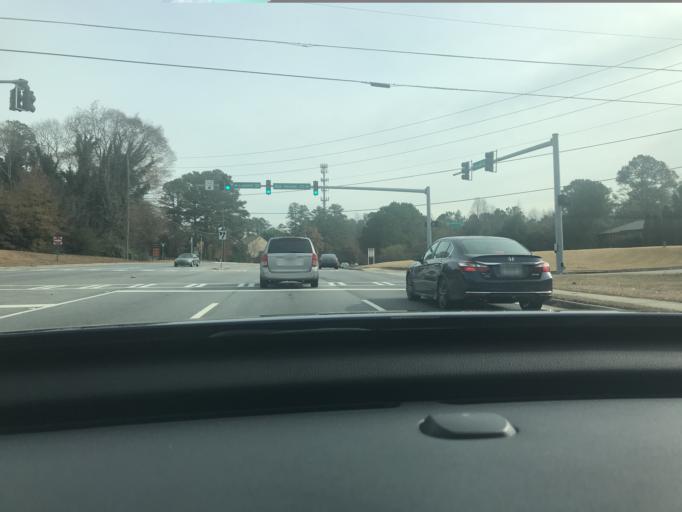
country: US
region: Georgia
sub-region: Gwinnett County
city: Lilburn
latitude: 33.9299
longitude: -84.1182
